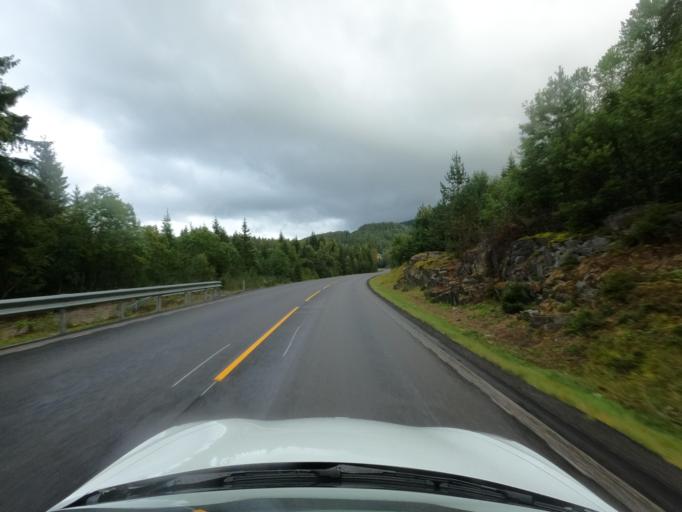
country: NO
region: Telemark
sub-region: Kviteseid
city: Kviteseid
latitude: 59.4435
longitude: 8.5149
